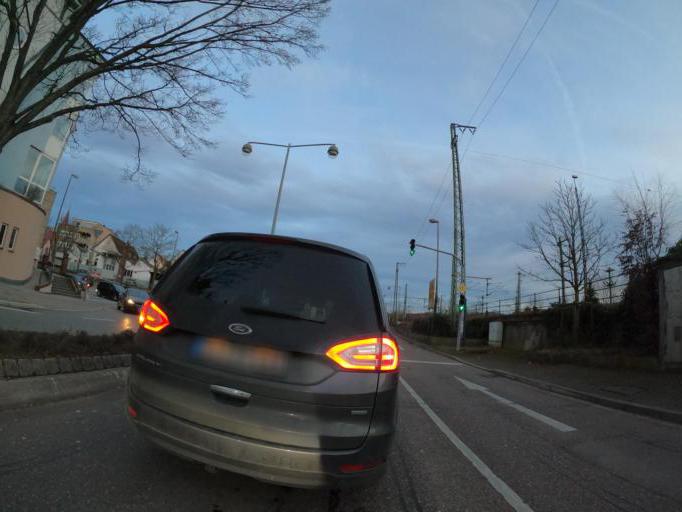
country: DE
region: Baden-Wuerttemberg
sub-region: Regierungsbezirk Stuttgart
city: Plochingen
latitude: 48.7098
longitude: 9.4157
